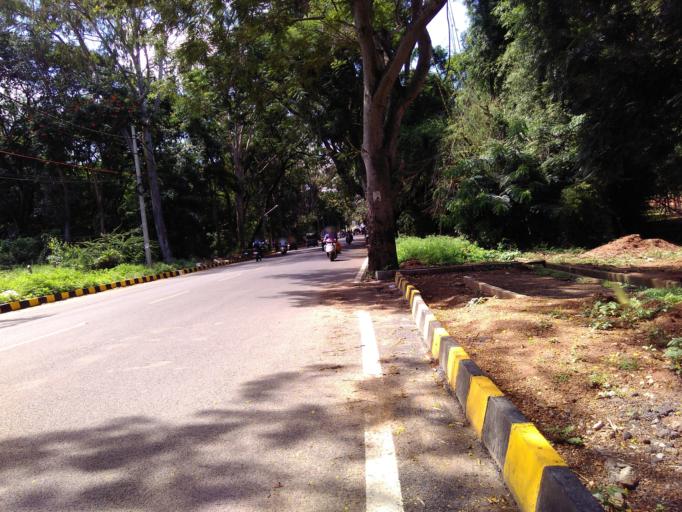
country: IN
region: Karnataka
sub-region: Mysore
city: Mysore
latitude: 12.3155
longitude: 76.6273
